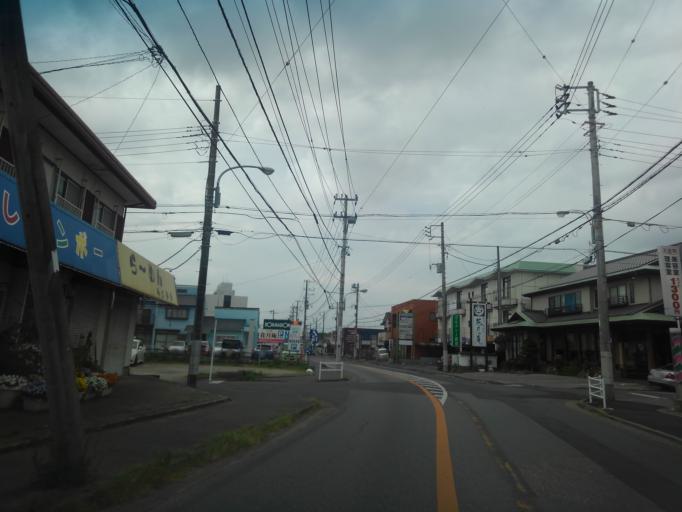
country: JP
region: Chiba
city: Kimitsu
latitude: 35.3290
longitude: 139.9066
